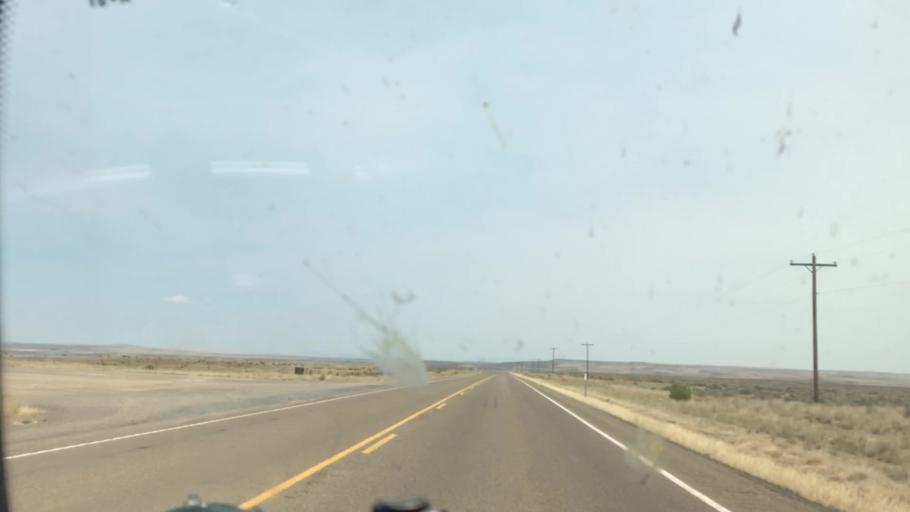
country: US
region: Idaho
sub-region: Owyhee County
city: Homedale
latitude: 42.8579
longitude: -117.5668
